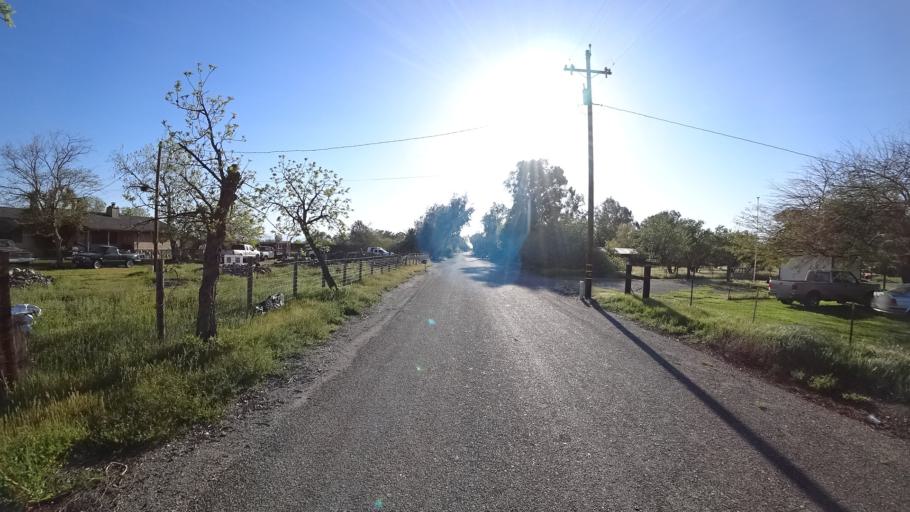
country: US
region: California
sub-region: Glenn County
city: Orland
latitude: 39.7696
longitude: -122.2272
